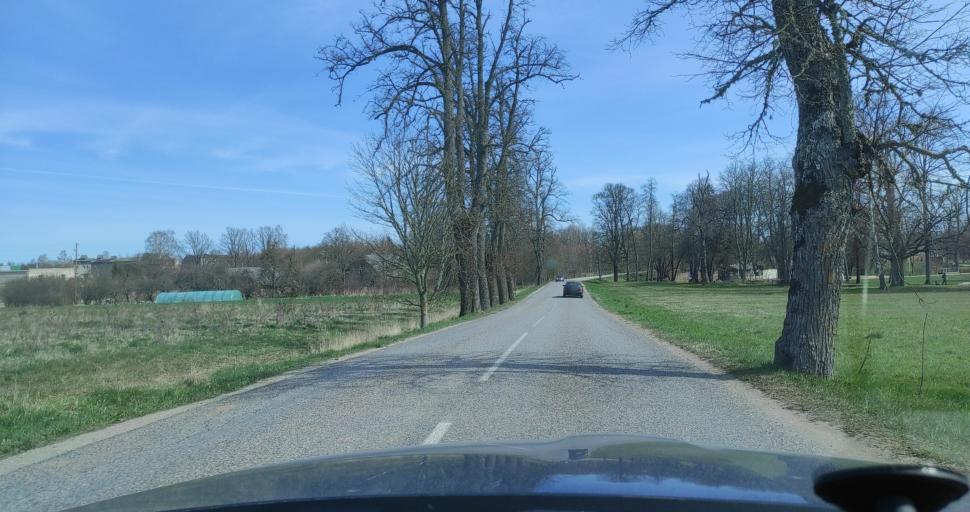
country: LV
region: Talsu Rajons
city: Talsi
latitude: 57.2235
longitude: 22.5131
